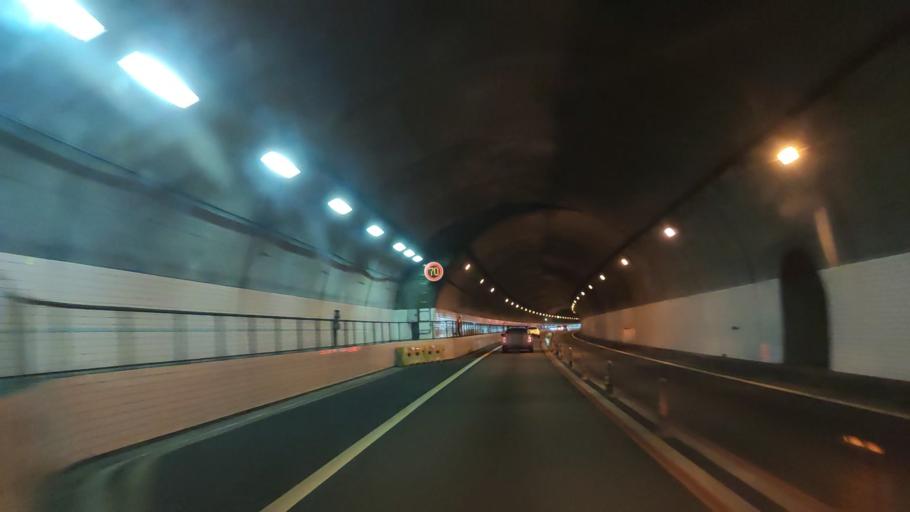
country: JP
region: Tokushima
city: Ikedacho
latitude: 34.0205
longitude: 133.8098
